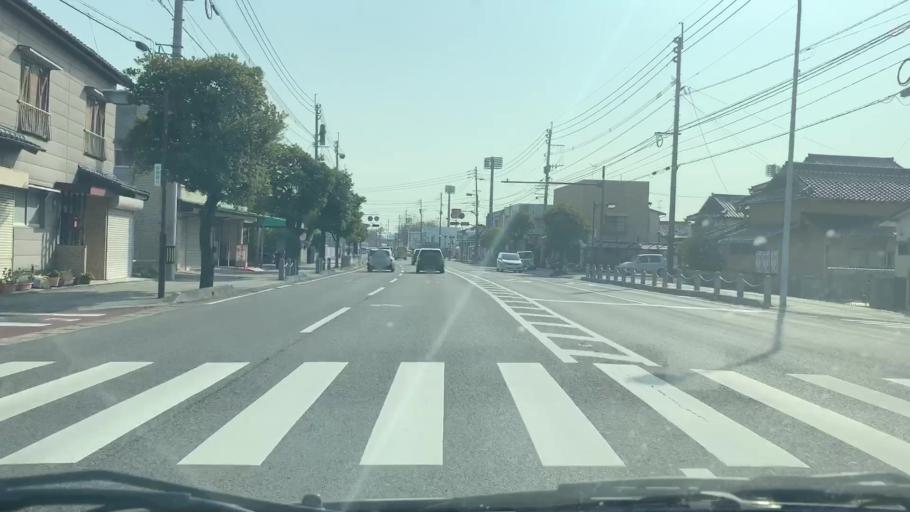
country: JP
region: Saga Prefecture
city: Saga-shi
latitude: 33.2806
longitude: 130.2922
